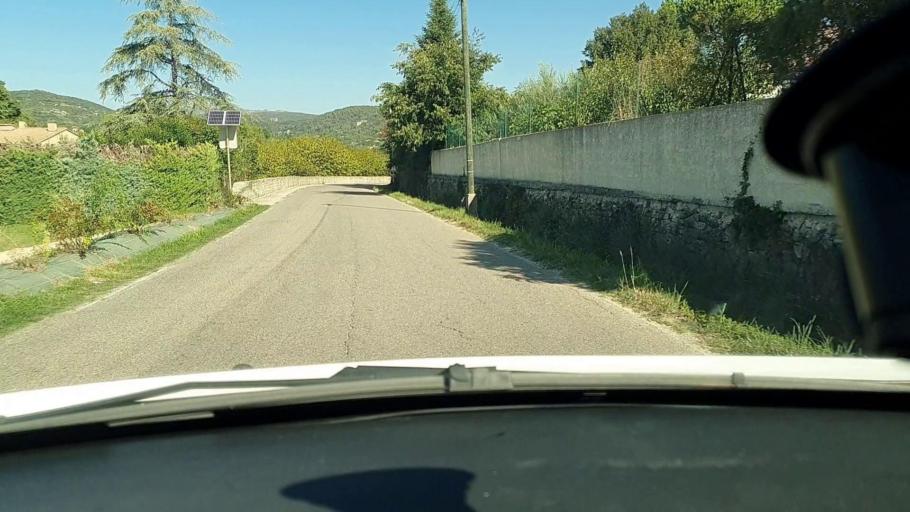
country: FR
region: Languedoc-Roussillon
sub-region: Departement du Gard
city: Saint-Julien-de-Peyrolas
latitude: 44.2906
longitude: 4.5652
